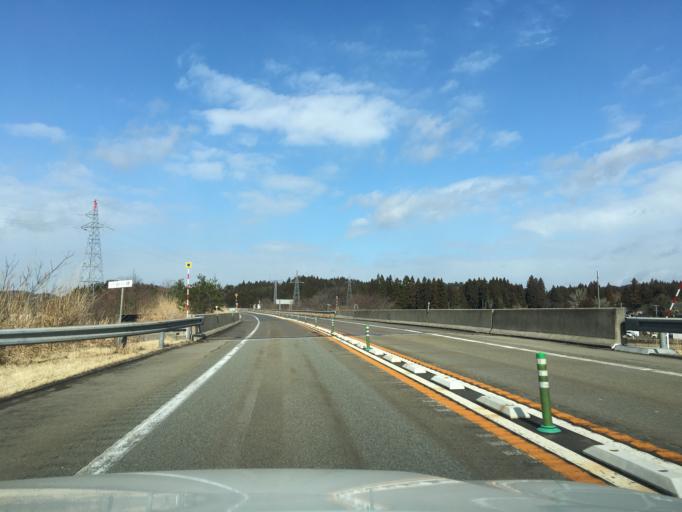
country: JP
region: Akita
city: Akita
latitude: 39.7372
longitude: 140.1734
